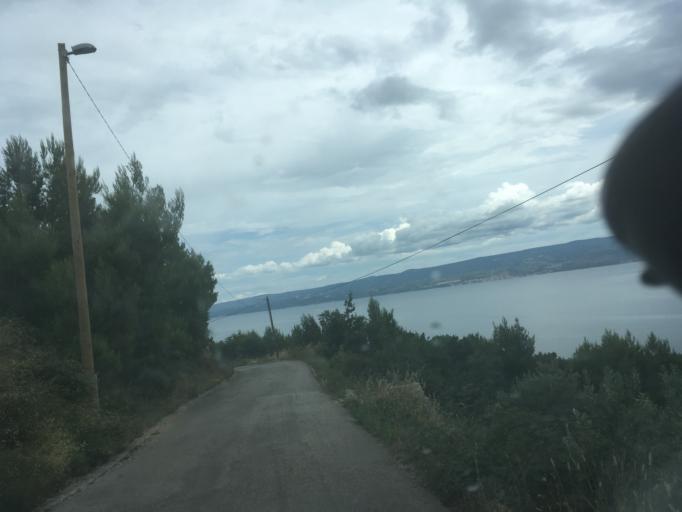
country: HR
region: Splitsko-Dalmatinska
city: Jesenice
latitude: 43.4590
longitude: 16.6171
